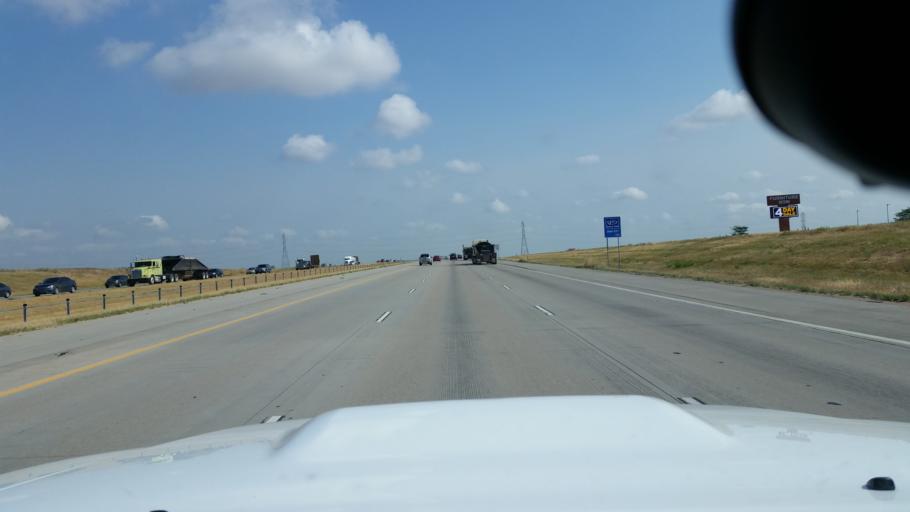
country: US
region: Colorado
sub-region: Weld County
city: Dacono
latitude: 40.0519
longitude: -104.9803
